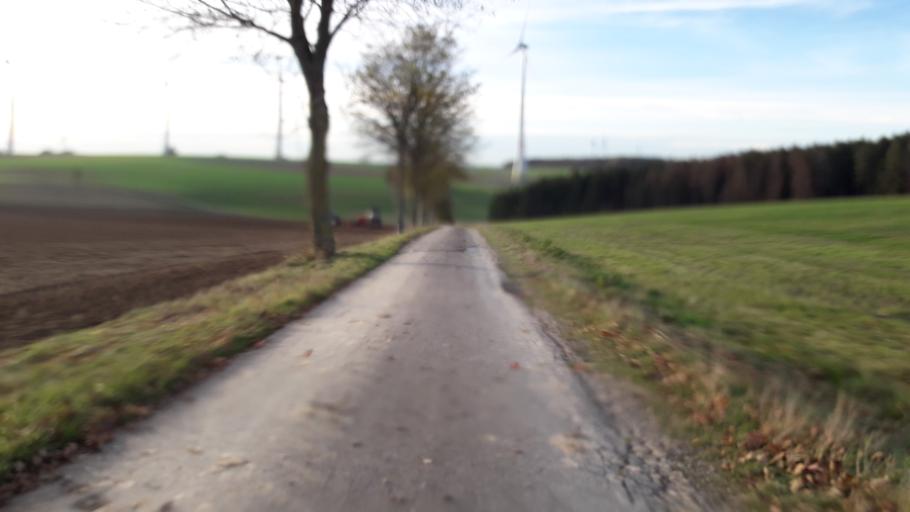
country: DE
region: North Rhine-Westphalia
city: Lichtenau
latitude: 51.6719
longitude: 8.8744
